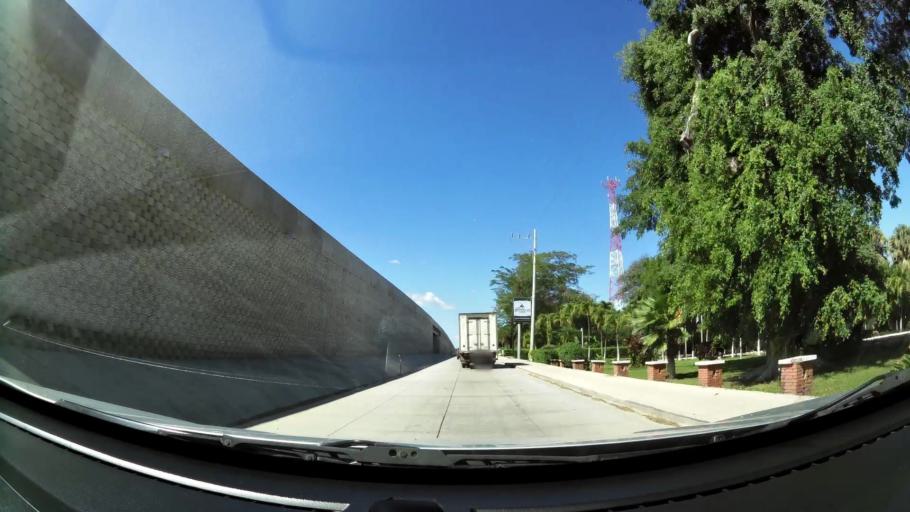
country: CR
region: Guanacaste
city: Liberia
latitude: 10.6112
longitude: -85.4335
